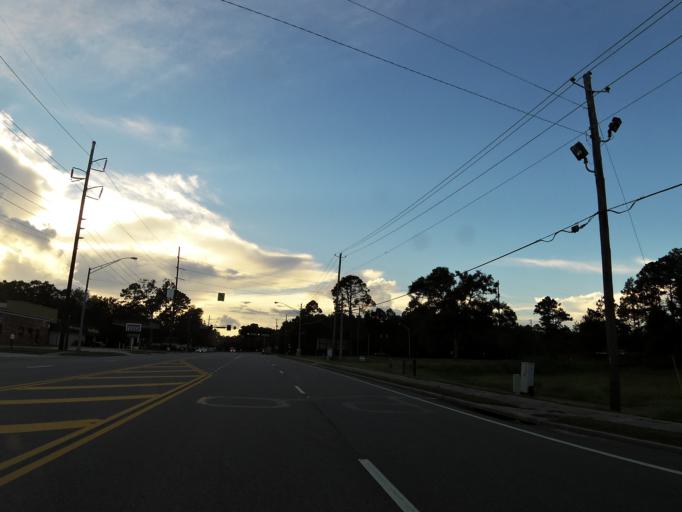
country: US
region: Georgia
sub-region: Camden County
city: St. Marys
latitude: 30.7423
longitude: -81.5530
